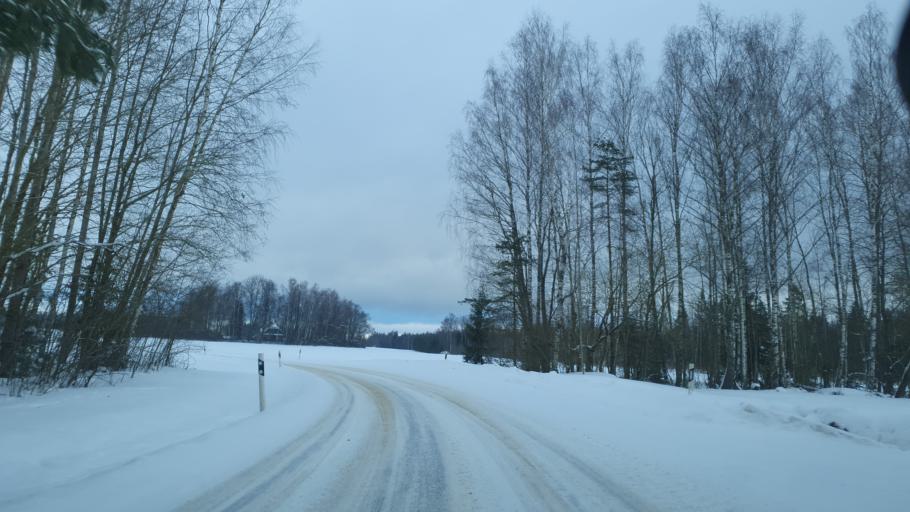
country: EE
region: Polvamaa
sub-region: Polva linn
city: Polva
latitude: 58.1308
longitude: 27.0945
